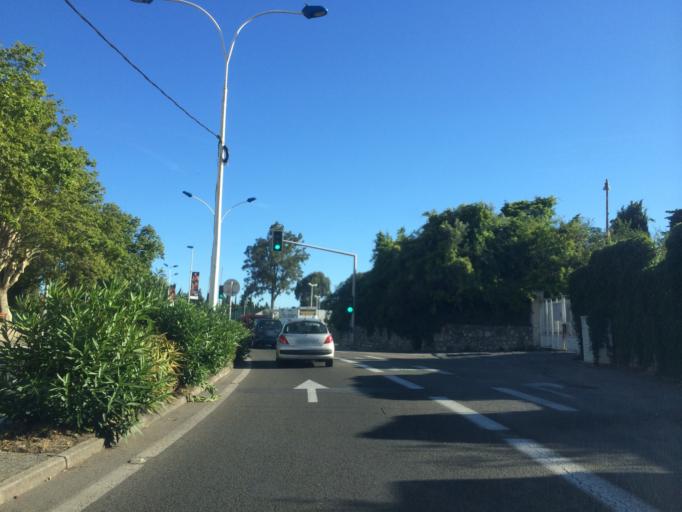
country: FR
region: Provence-Alpes-Cote d'Azur
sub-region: Departement des Alpes-Maritimes
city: Antibes
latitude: 43.5913
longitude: 7.1244
